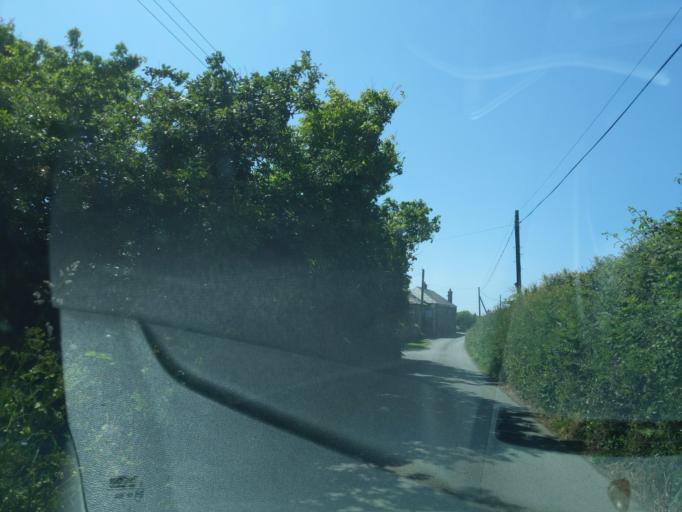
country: GB
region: England
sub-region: Cornwall
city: Wadebridge
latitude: 50.5840
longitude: -4.8464
